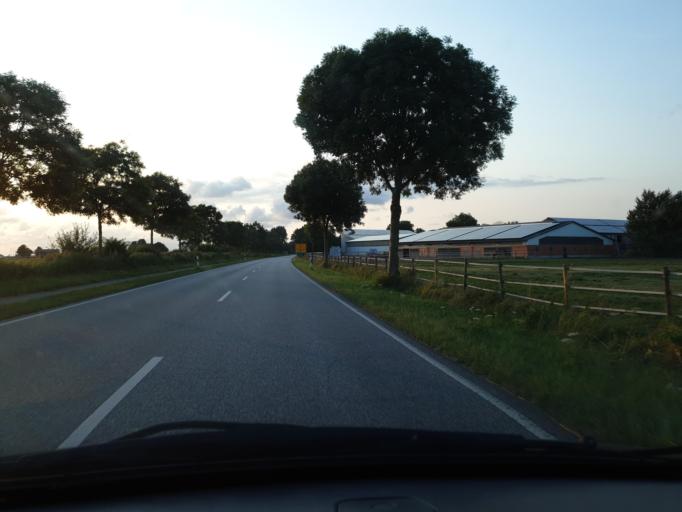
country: DE
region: Schleswig-Holstein
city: Schmedeswurth
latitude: 53.9144
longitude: 9.0513
